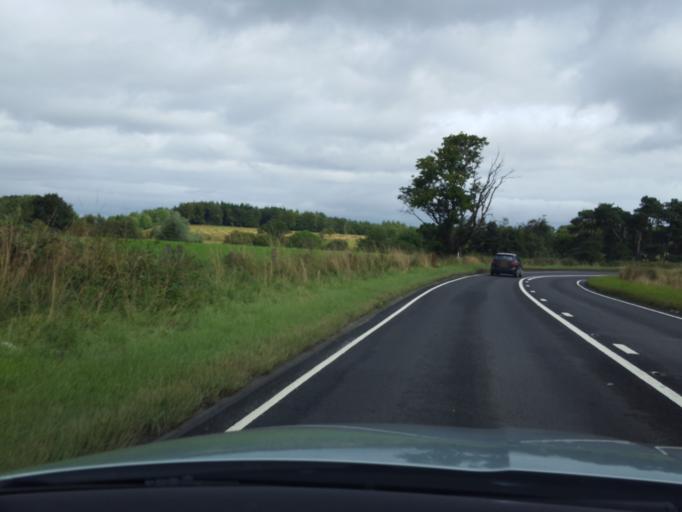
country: GB
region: Scotland
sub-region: West Lothian
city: Bathgate
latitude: 55.9340
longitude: -3.6769
